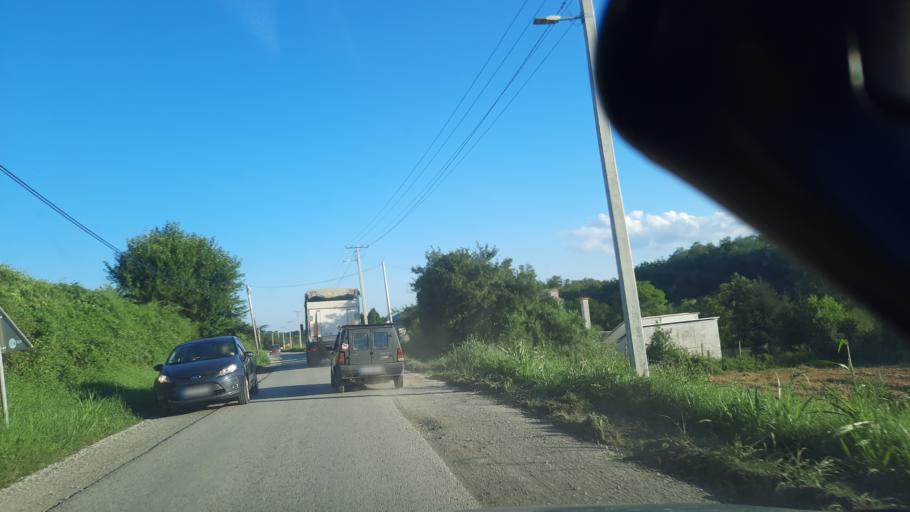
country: RS
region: Autonomna Pokrajina Vojvodina
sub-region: Juznobacki Okrug
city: Sremski Karlovci
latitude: 45.1215
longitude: 19.9438
